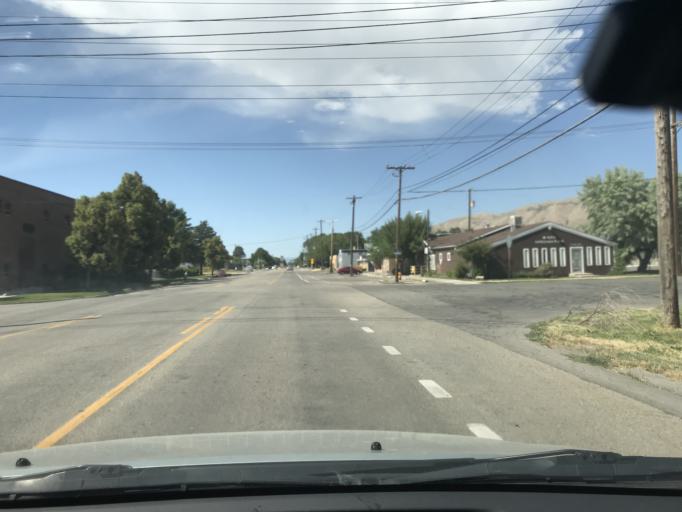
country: US
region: Utah
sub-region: Salt Lake County
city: Salt Lake City
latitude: 40.7669
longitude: -111.9196
